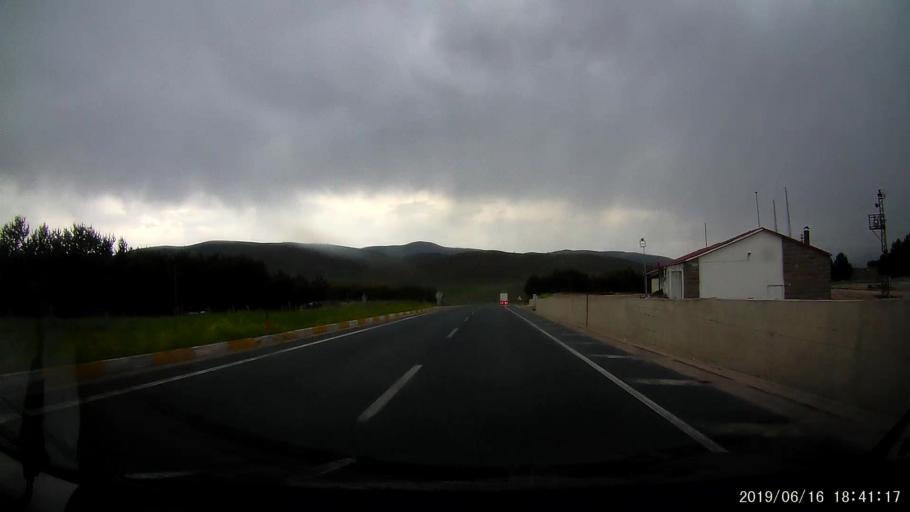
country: TR
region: Erzincan
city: Catalarmut
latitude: 39.8750
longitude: 39.1307
